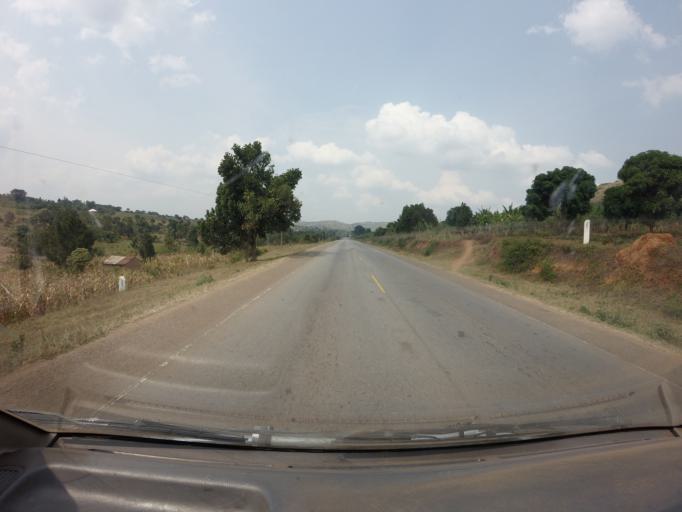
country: UG
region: Central Region
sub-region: Lyantonde District
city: Lyantonde
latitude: -0.3796
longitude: 31.2409
